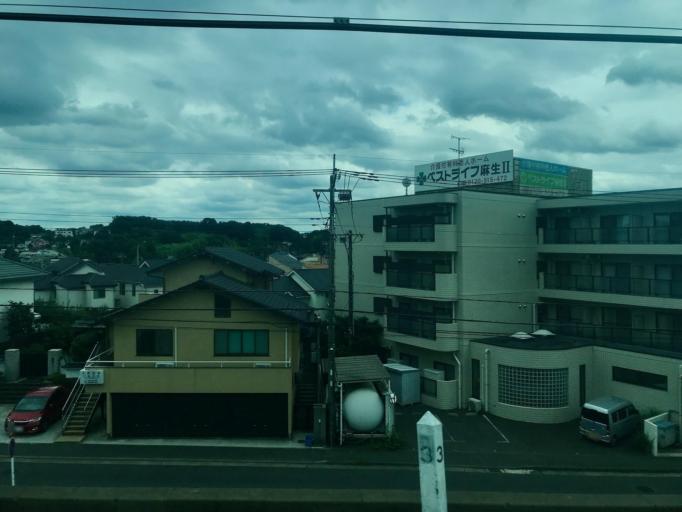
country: JP
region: Tokyo
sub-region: Machida-shi
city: Machida
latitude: 35.6070
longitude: 139.4791
